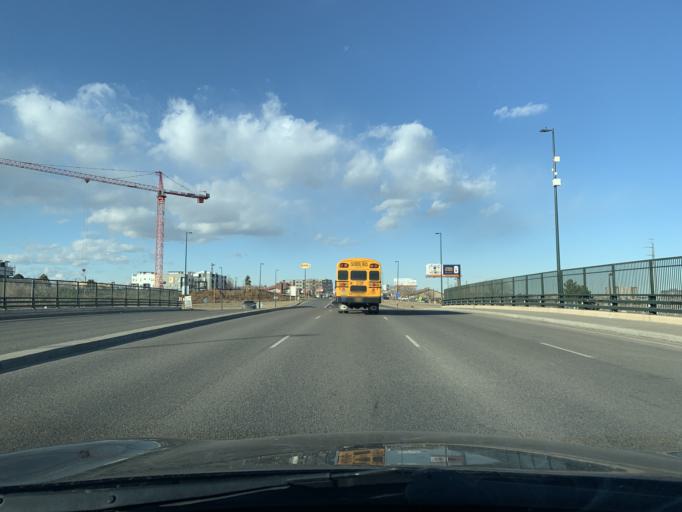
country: US
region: Colorado
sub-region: Denver County
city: Denver
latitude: 39.7401
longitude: -105.0251
